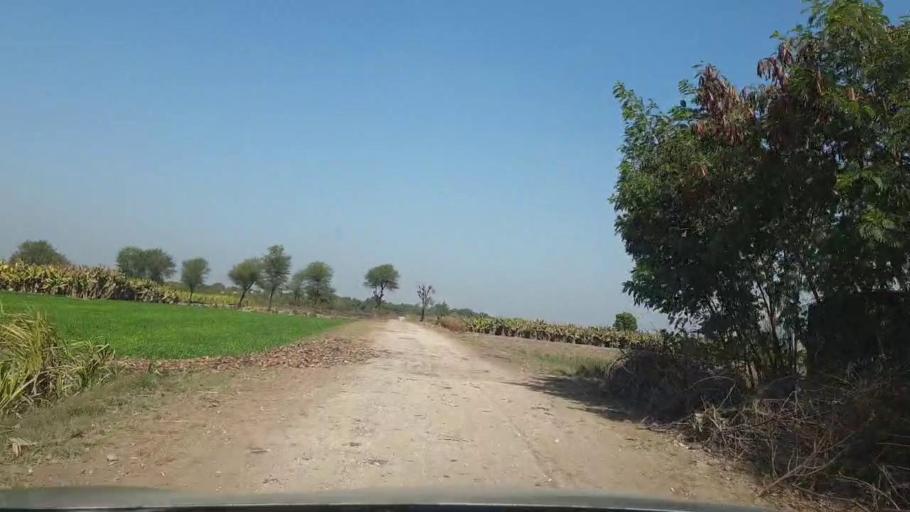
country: PK
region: Sindh
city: Tando Adam
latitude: 25.6172
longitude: 68.6462
